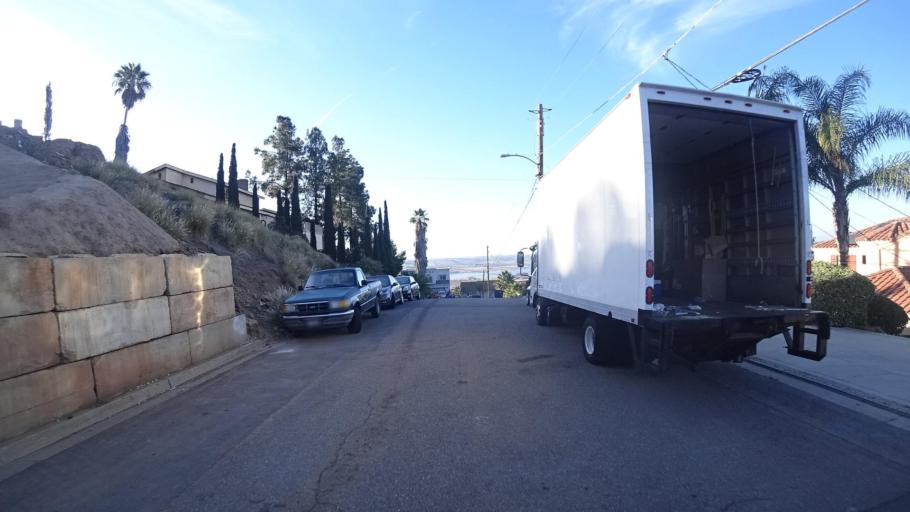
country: US
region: California
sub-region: San Diego County
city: La Presa
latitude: 32.7208
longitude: -116.9882
